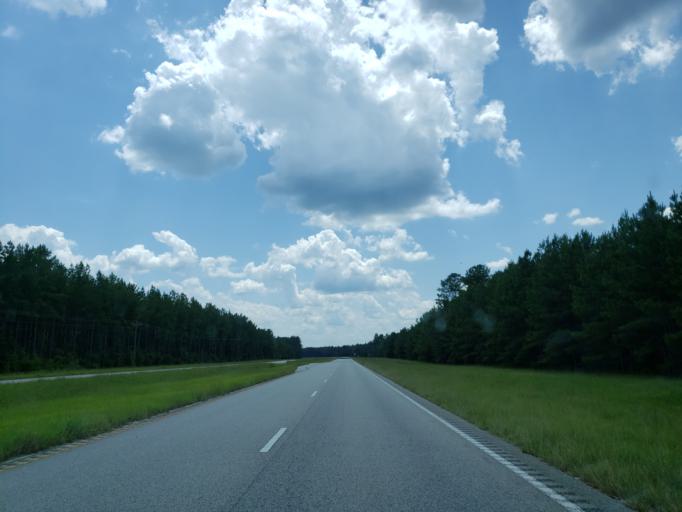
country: US
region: Mississippi
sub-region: Greene County
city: Leakesville
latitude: 31.2566
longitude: -88.5211
